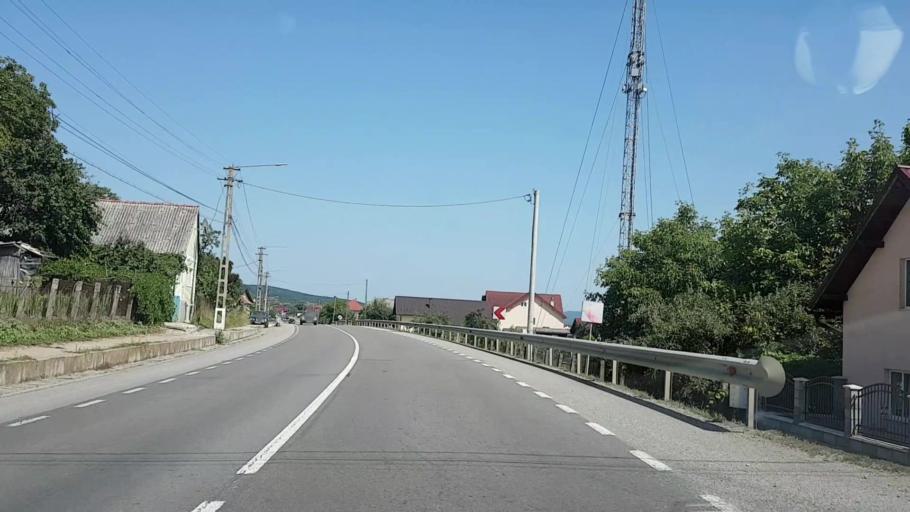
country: RO
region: Bistrita-Nasaud
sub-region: Comuna Uriu
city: Cristestii Ciceului
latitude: 47.1894
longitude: 24.1037
